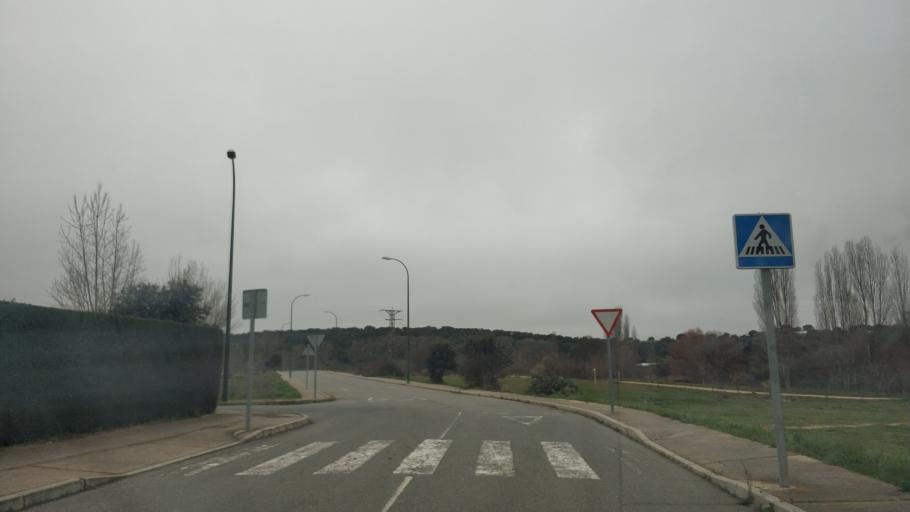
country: ES
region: Castille and Leon
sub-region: Provincia de Salamanca
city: Villamayor
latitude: 40.9995
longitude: -5.7267
